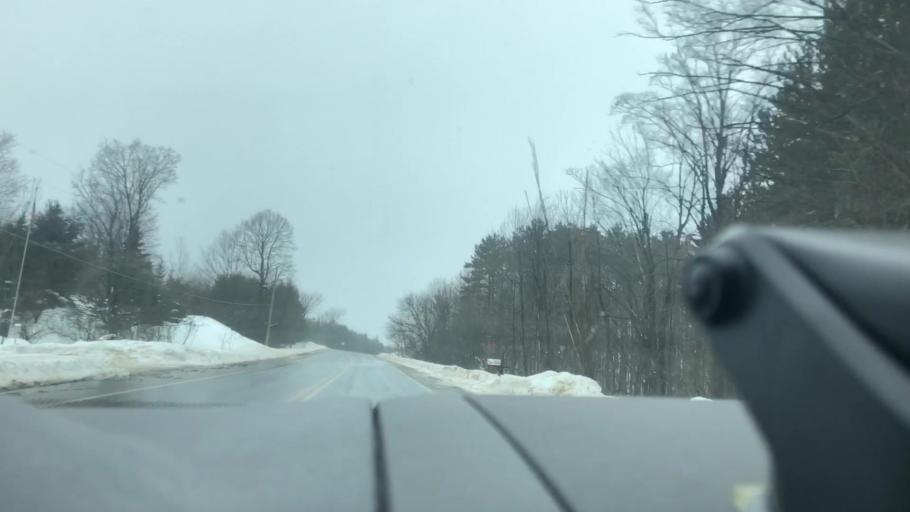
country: US
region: Michigan
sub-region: Charlevoix County
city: East Jordan
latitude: 45.1572
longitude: -85.1581
